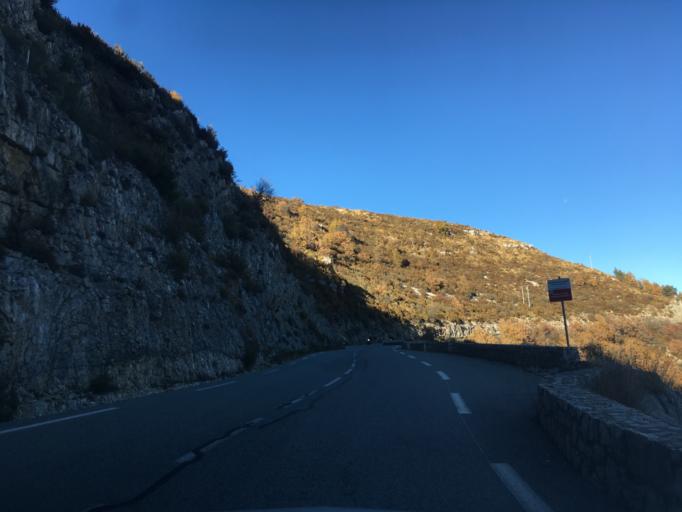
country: FR
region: Provence-Alpes-Cote d'Azur
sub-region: Departement du Var
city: Montferrat
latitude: 43.6780
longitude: 6.5069
